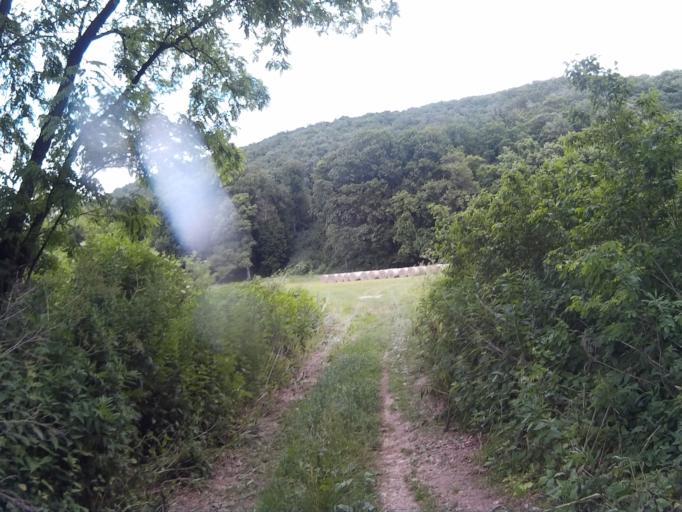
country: HU
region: Veszprem
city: Herend
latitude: 47.1014
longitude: 17.7460
